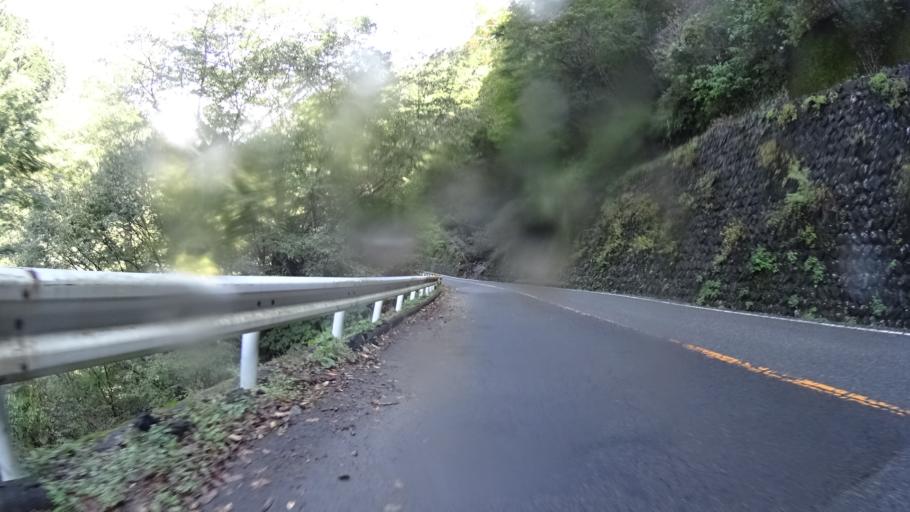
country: JP
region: Yamanashi
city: Enzan
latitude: 35.7983
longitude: 138.8655
